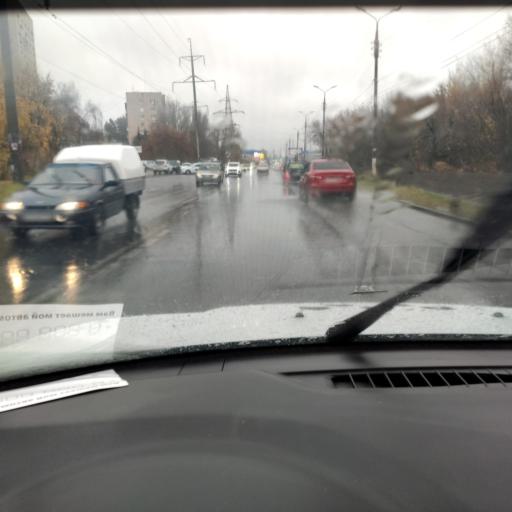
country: RU
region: Samara
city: Tol'yatti
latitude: 53.5269
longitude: 49.3964
